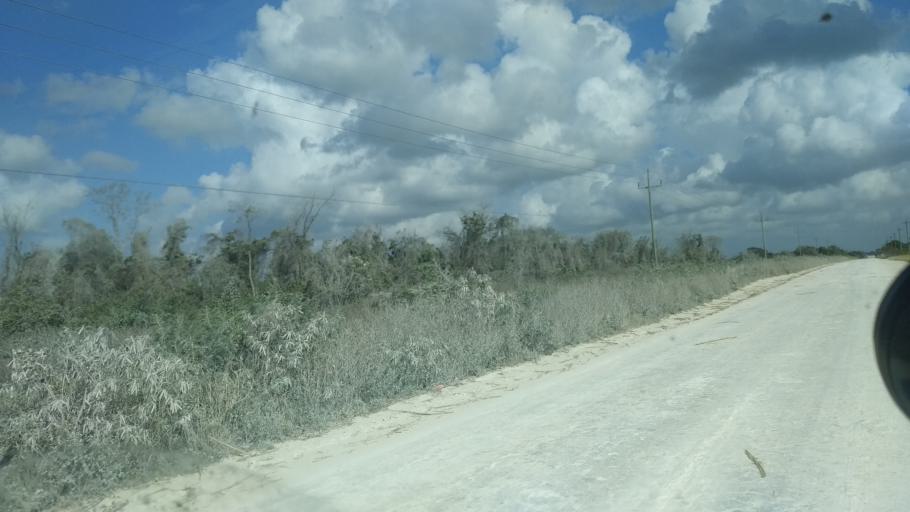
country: BZ
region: Corozal
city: Corozal
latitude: 18.3295
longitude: -88.4947
